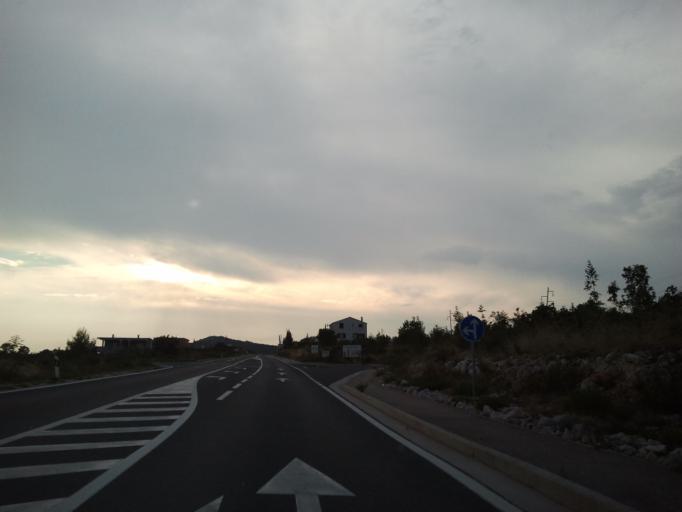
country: HR
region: Zadarska
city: Posedarje
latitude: 44.2200
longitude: 15.4550
